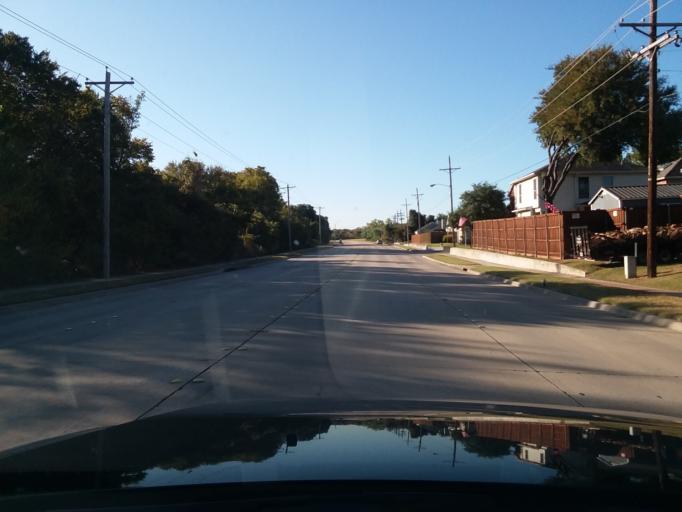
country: US
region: Texas
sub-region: Denton County
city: Lewisville
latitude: 33.0232
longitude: -97.0280
